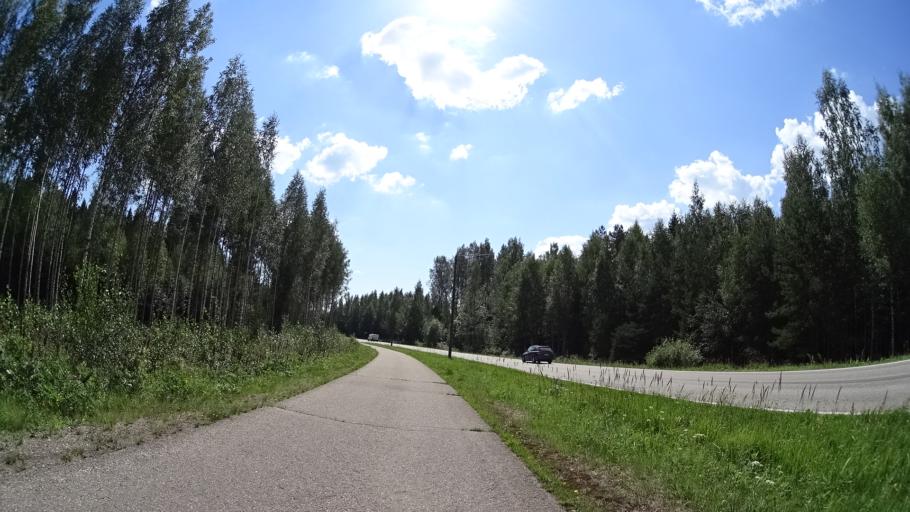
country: FI
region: Uusimaa
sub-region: Helsinki
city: Tuusula
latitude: 60.3519
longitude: 24.9964
